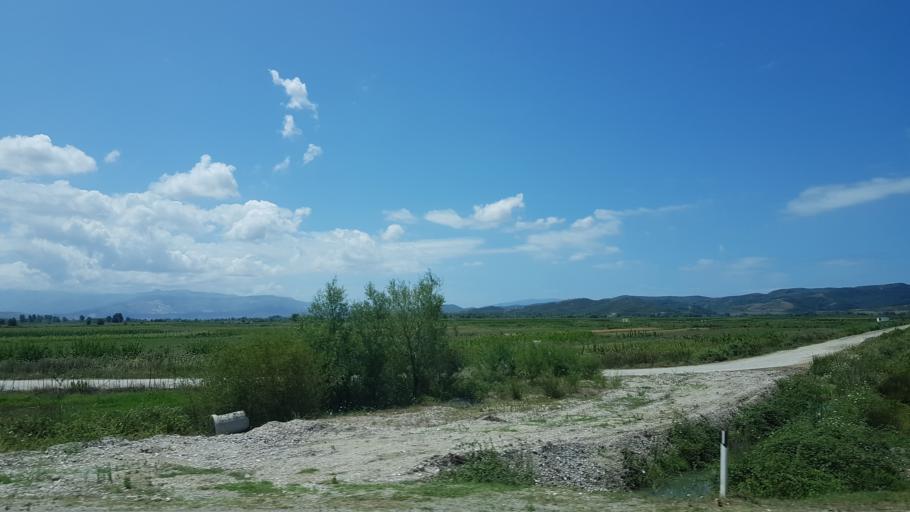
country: AL
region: Fier
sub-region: Rrethi i Fierit
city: Cakran
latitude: 40.5956
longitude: 19.5715
